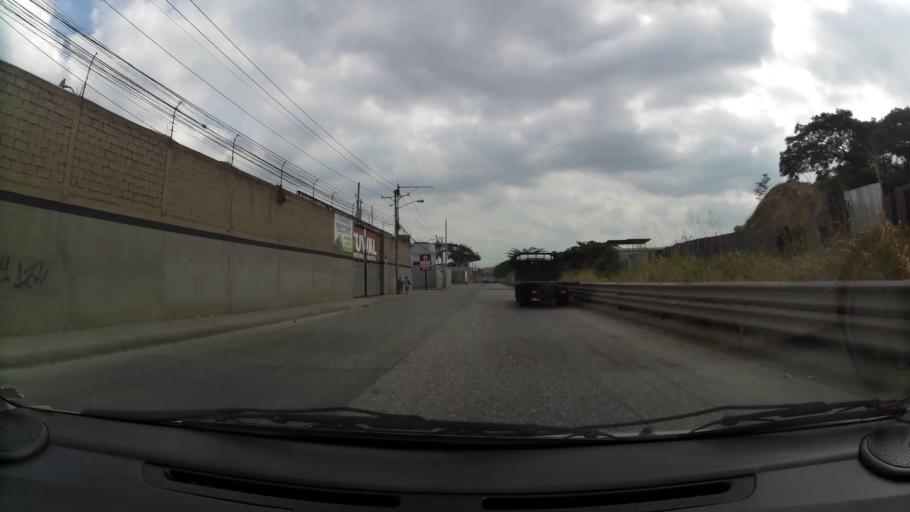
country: EC
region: Guayas
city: Santa Lucia
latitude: -2.1014
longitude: -79.9422
